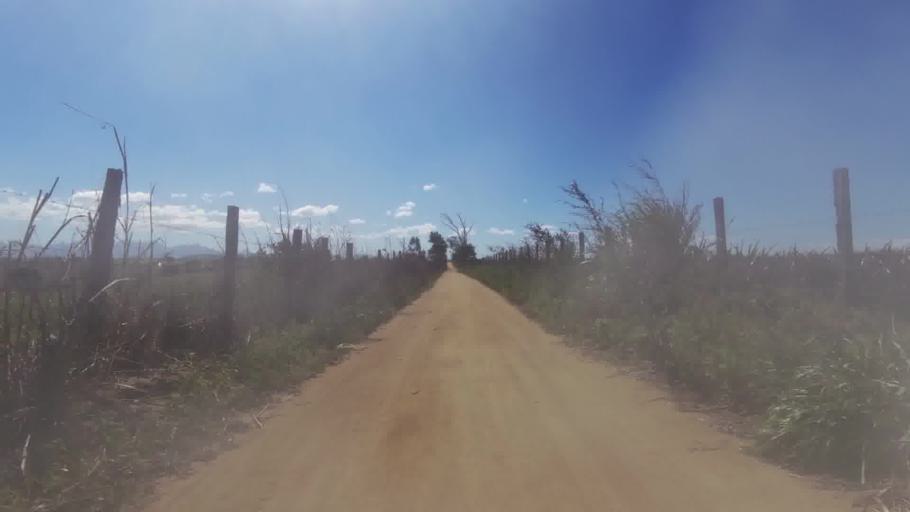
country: BR
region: Espirito Santo
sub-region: Marataizes
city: Marataizes
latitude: -21.1588
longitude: -40.9644
